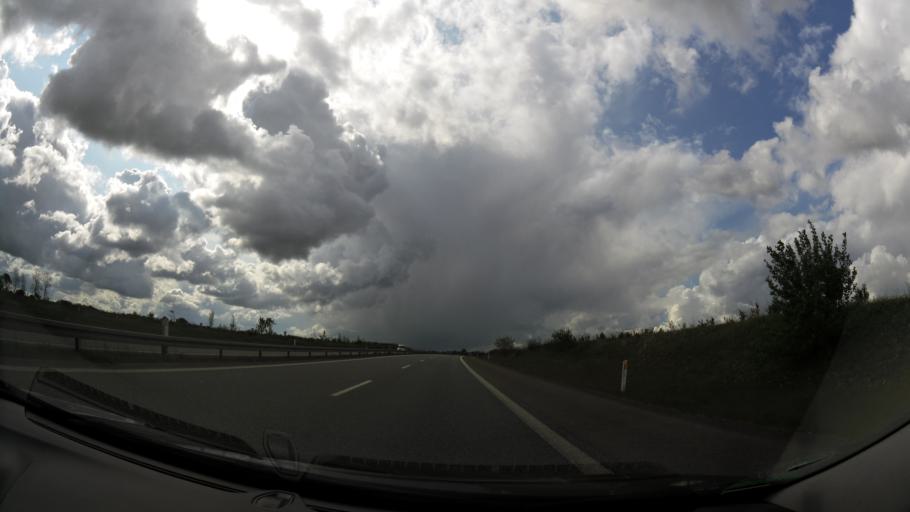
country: DK
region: South Denmark
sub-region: Faaborg-Midtfyn Kommune
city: Ringe
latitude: 55.2224
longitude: 10.5001
